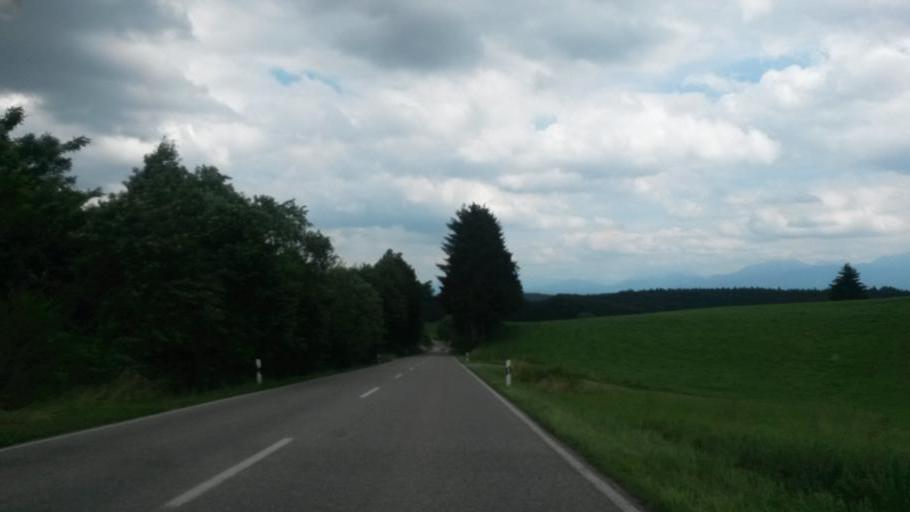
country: DE
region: Bavaria
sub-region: Upper Bavaria
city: Rimsting
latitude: 47.9083
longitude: 12.3279
